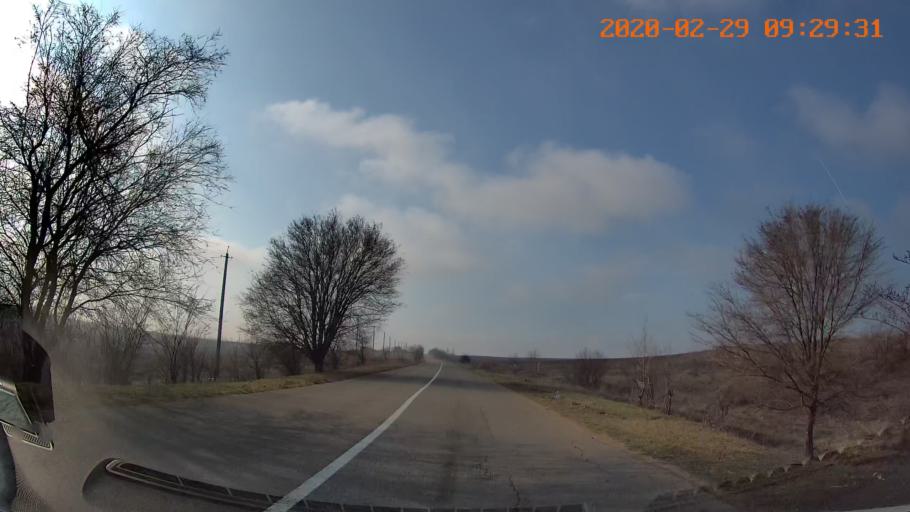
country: UA
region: Odessa
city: Lymanske
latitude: 46.6774
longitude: 29.9208
